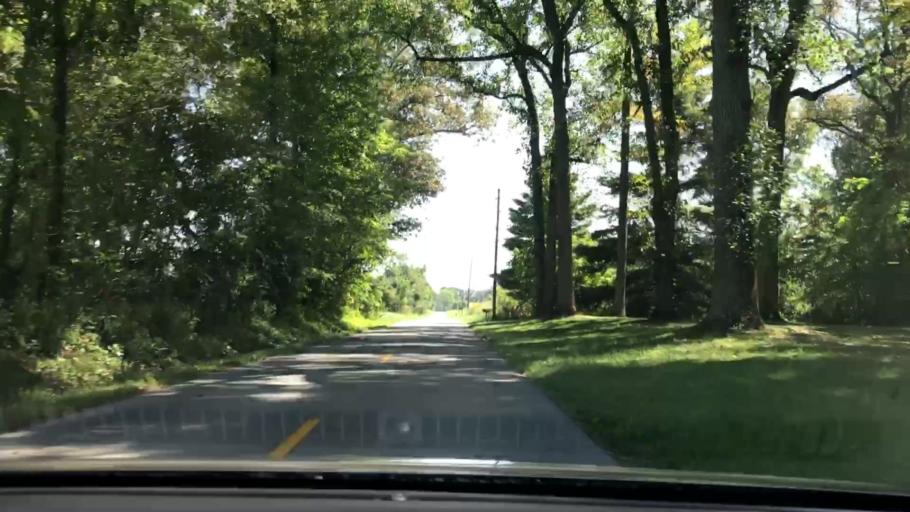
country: US
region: Kentucky
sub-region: Fulton County
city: Fulton
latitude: 36.5218
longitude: -88.8963
